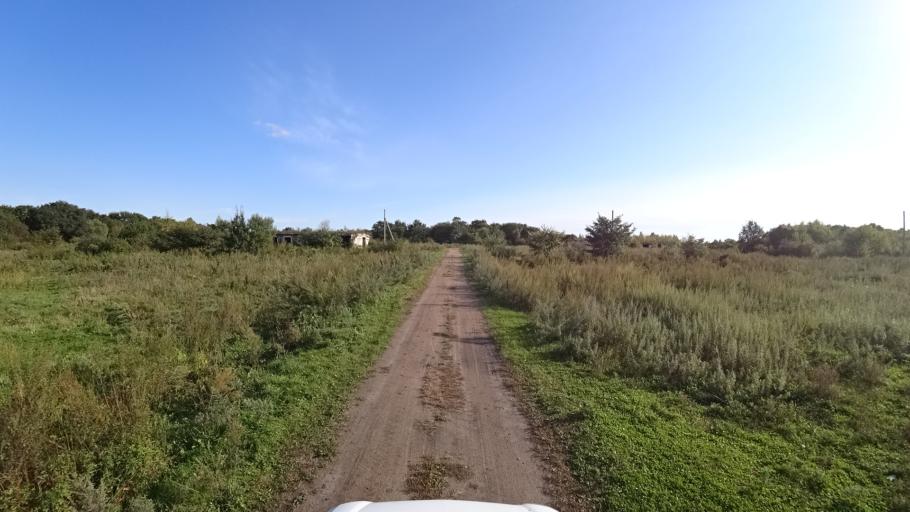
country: RU
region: Amur
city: Arkhara
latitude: 49.3482
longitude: 130.1067
